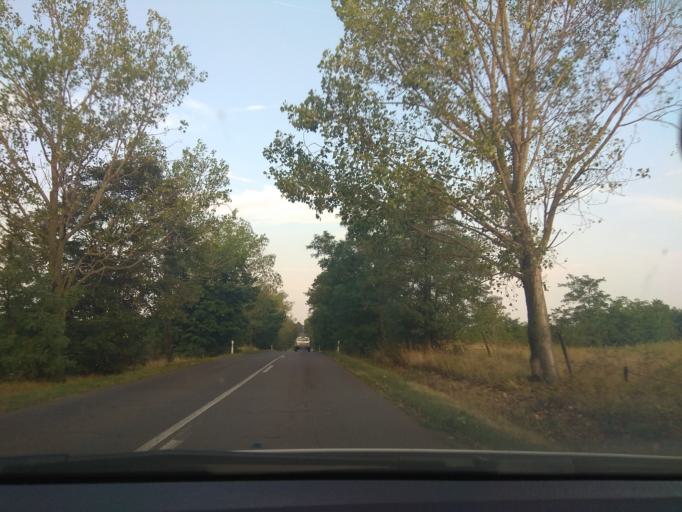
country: HU
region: Heves
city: Andornaktalya
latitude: 47.8309
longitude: 20.4494
